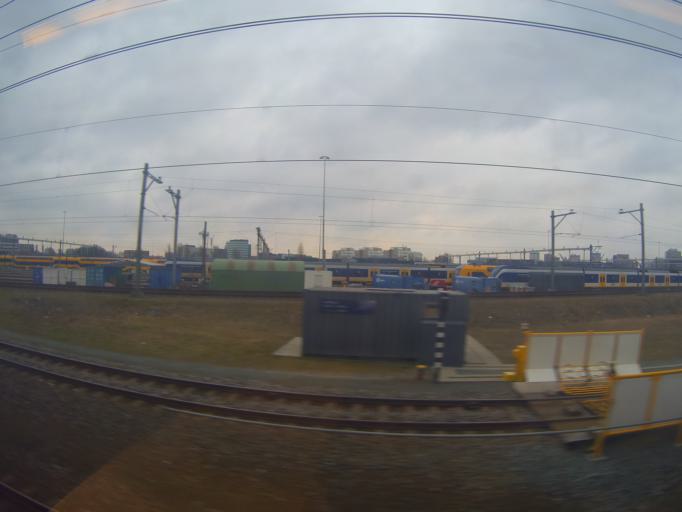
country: NL
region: South Holland
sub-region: Gemeente Leidschendam-Voorburg
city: Voorburg
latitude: 52.0736
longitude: 4.3386
